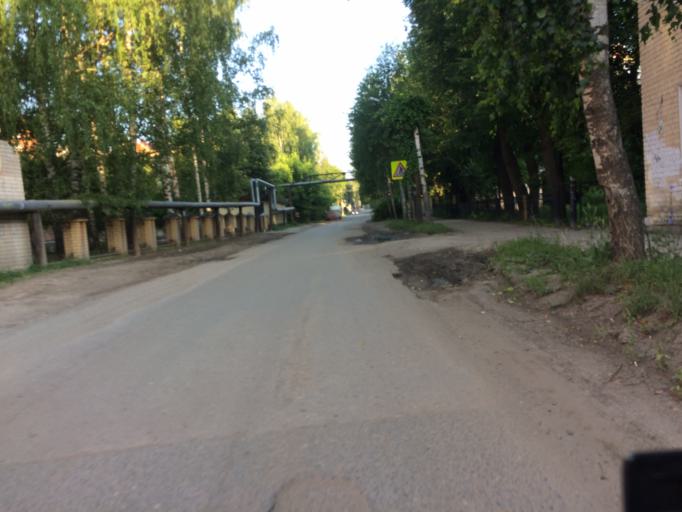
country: RU
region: Mariy-El
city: Yoshkar-Ola
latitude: 56.6435
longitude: 47.8933
